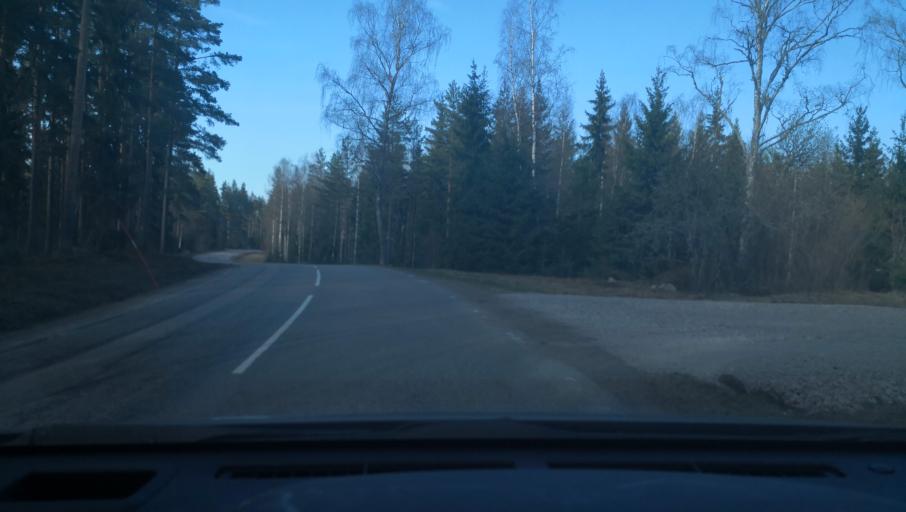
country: SE
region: Uppsala
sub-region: Heby Kommun
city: Morgongava
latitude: 60.0049
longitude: 16.9340
